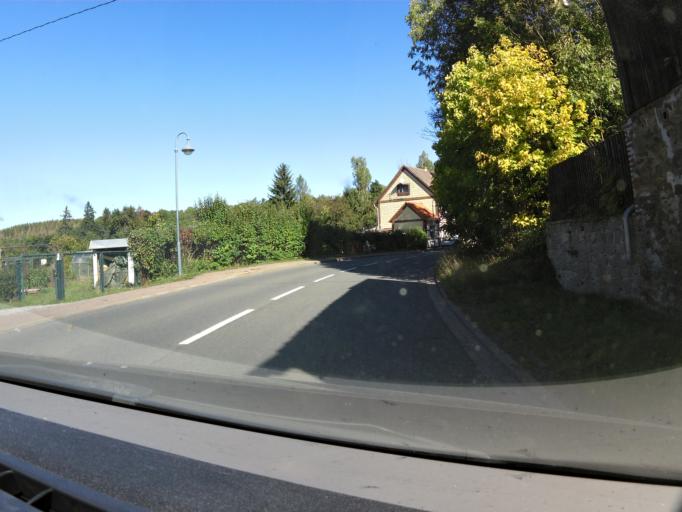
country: DE
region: Saxony-Anhalt
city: Hasselfelde
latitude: 51.6686
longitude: 10.8847
